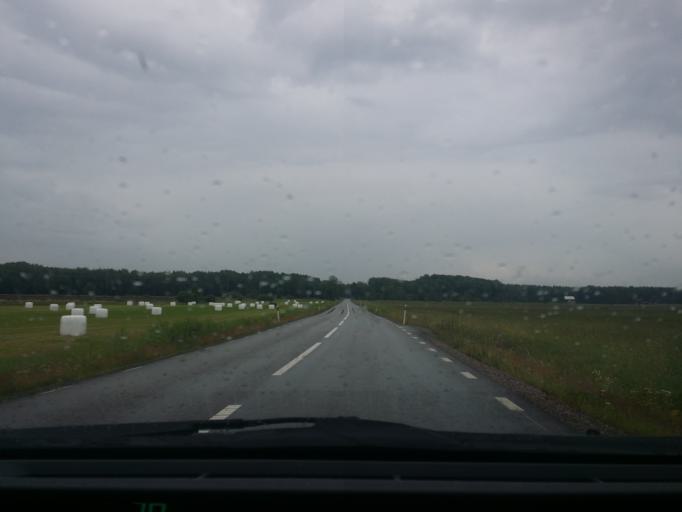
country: SE
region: OErebro
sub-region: Lindesbergs Kommun
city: Fellingsbro
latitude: 59.4227
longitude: 15.6531
